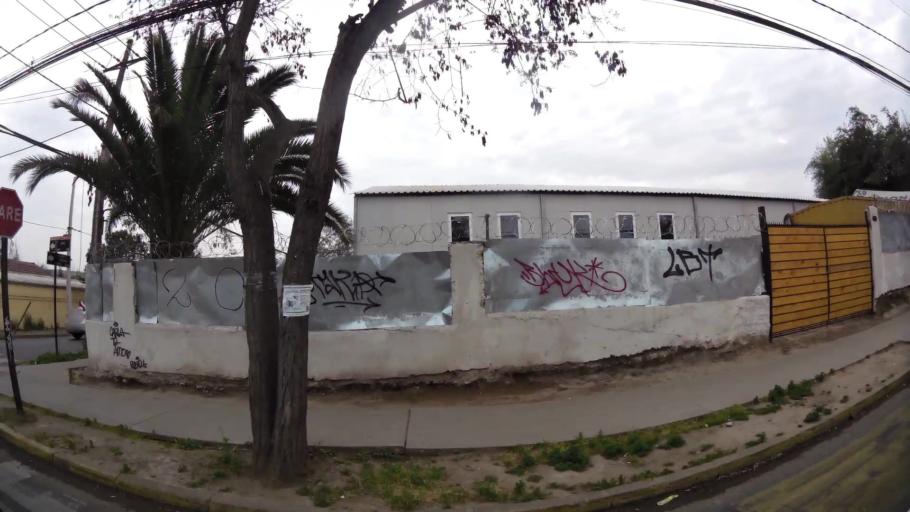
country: CL
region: Santiago Metropolitan
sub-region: Provincia de Santiago
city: Lo Prado
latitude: -33.5036
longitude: -70.7600
